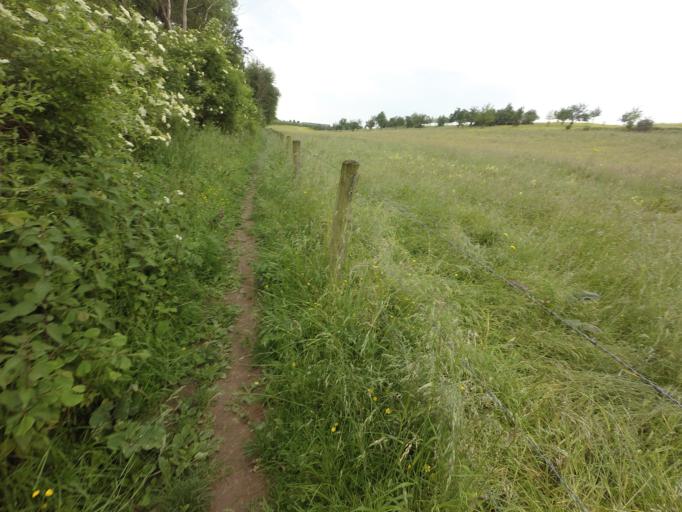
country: NL
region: Limburg
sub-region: Gemeente Voerendaal
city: Ubachsberg
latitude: 50.8523
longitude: 5.9674
